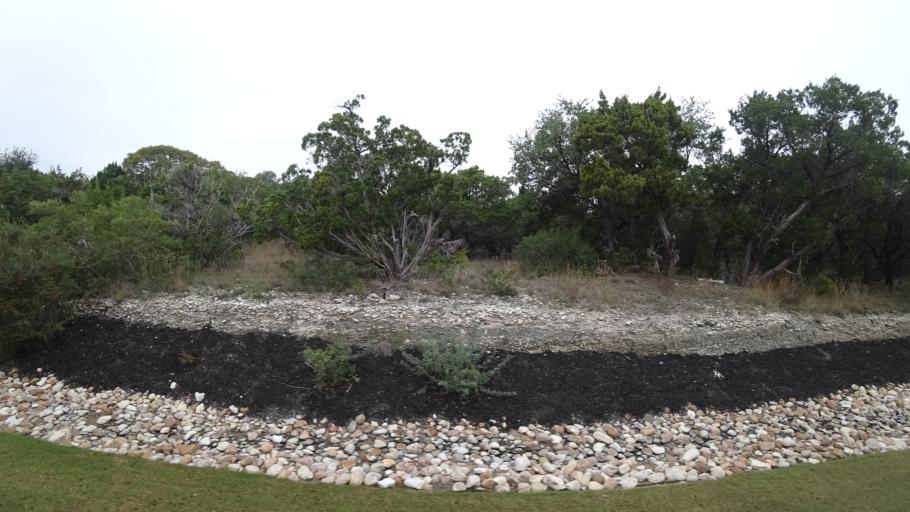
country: US
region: Texas
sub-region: Travis County
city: Hudson Bend
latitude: 30.3948
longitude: -97.9156
